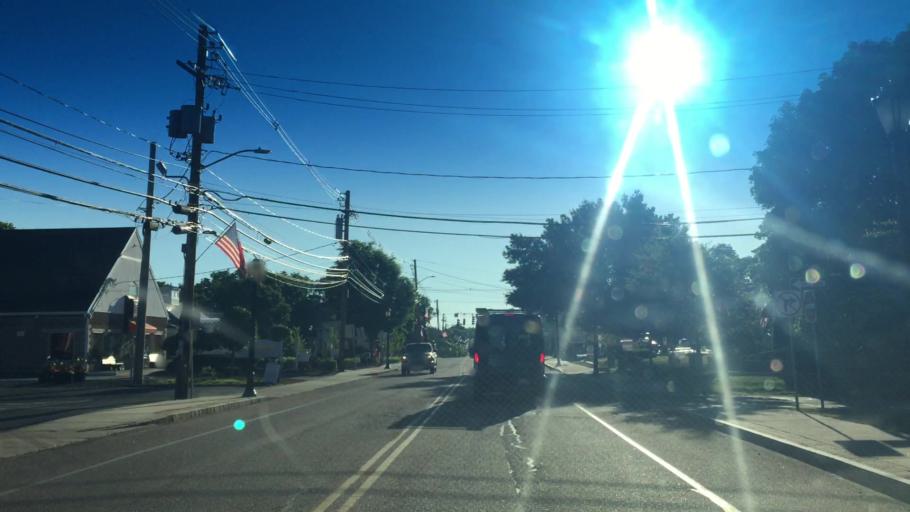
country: US
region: Massachusetts
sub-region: Norfolk County
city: Millis
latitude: 42.1669
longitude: -71.3587
